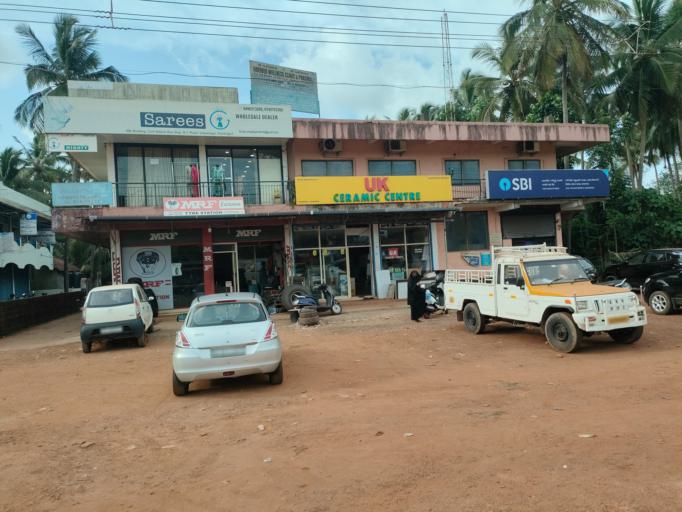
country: IN
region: Kerala
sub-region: Kasaragod District
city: Kasaragod
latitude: 12.5177
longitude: 75.0168
